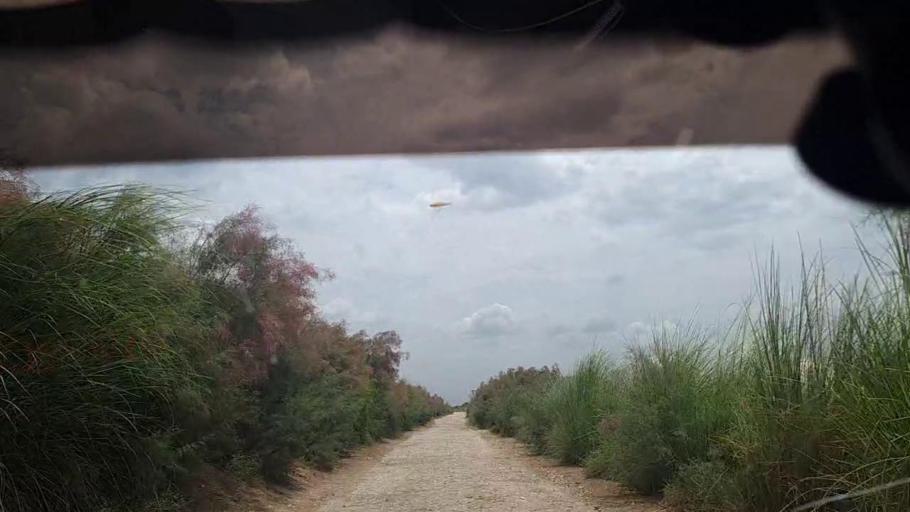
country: PK
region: Sindh
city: Rustam jo Goth
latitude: 28.0581
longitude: 68.9399
